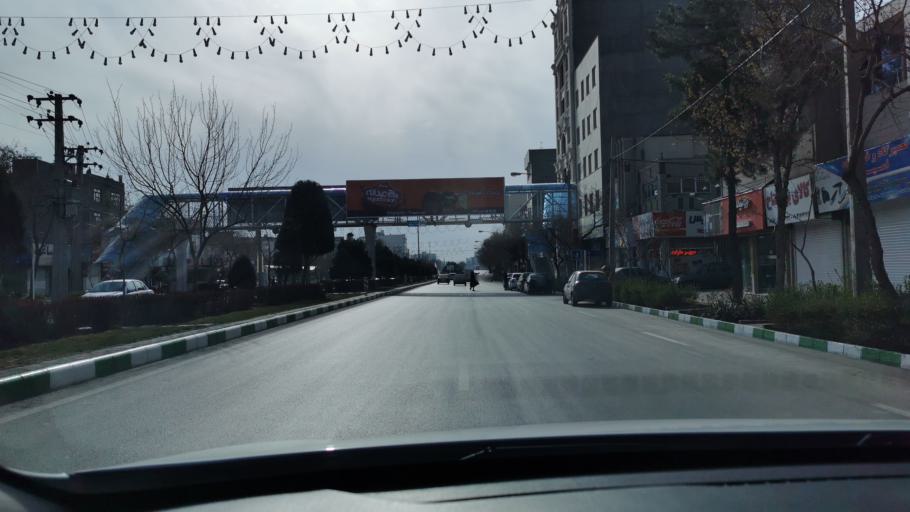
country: IR
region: Razavi Khorasan
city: Mashhad
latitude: 36.2971
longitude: 59.5273
